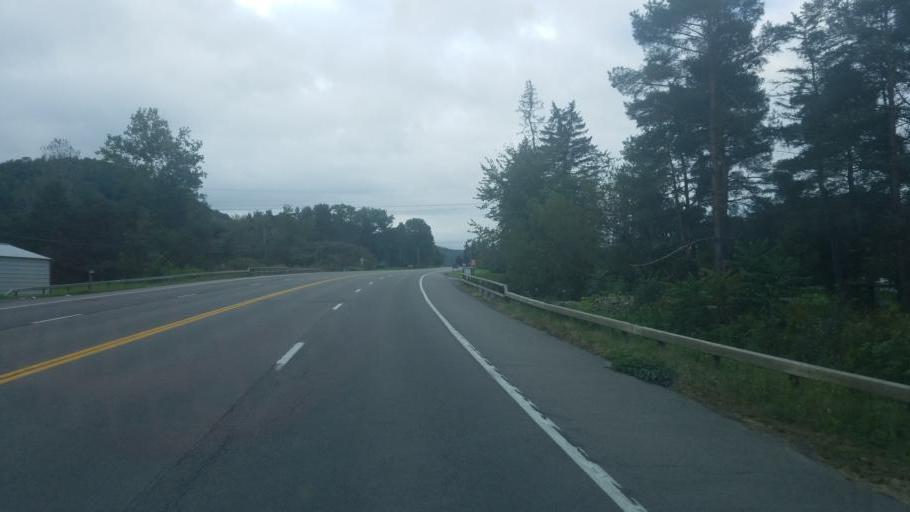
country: US
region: New York
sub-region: Cattaraugus County
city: Weston Mills
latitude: 42.1557
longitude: -78.3973
